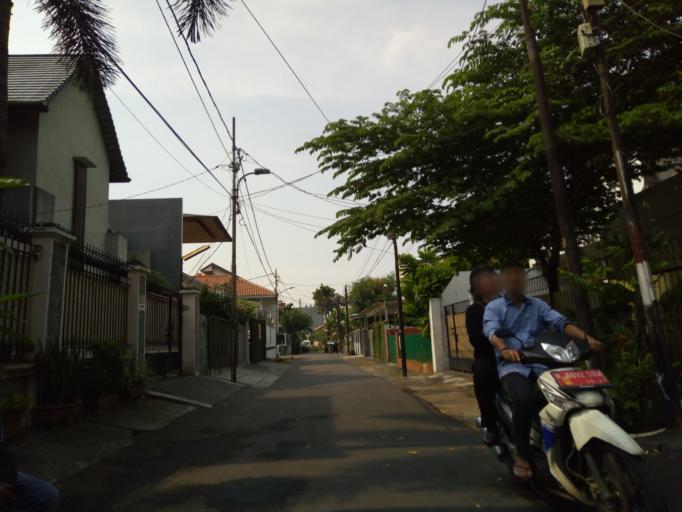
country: ID
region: Jakarta Raya
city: Jakarta
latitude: -6.2080
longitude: 106.8341
